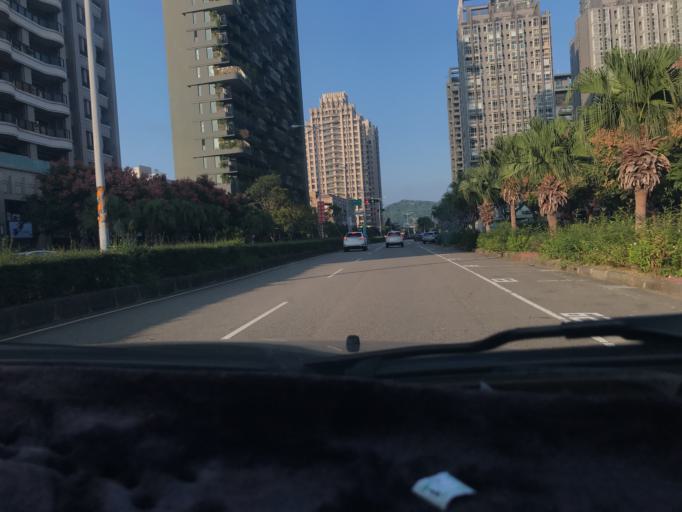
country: TW
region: Taiwan
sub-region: Hsinchu
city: Zhubei
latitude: 24.8103
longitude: 121.0340
